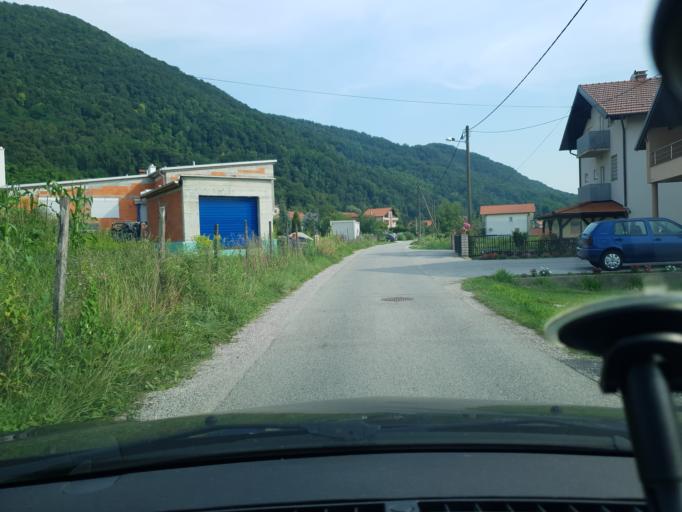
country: HR
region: Zagrebacka
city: Jablanovec
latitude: 45.8748
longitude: 15.8453
